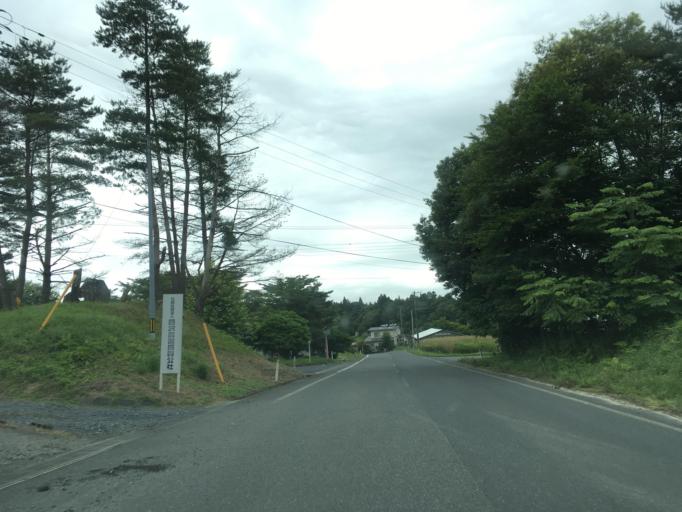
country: JP
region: Iwate
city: Ichinoseki
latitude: 38.8358
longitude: 141.3504
